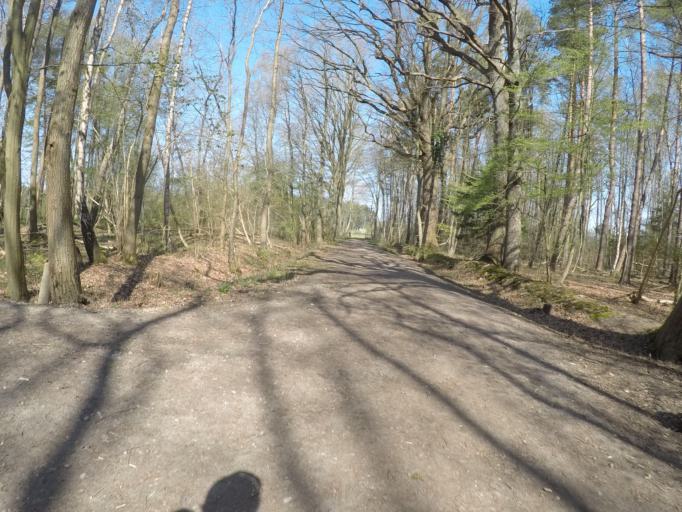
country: DE
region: Schleswig-Holstein
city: Rellingen
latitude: 53.6129
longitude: 9.7813
